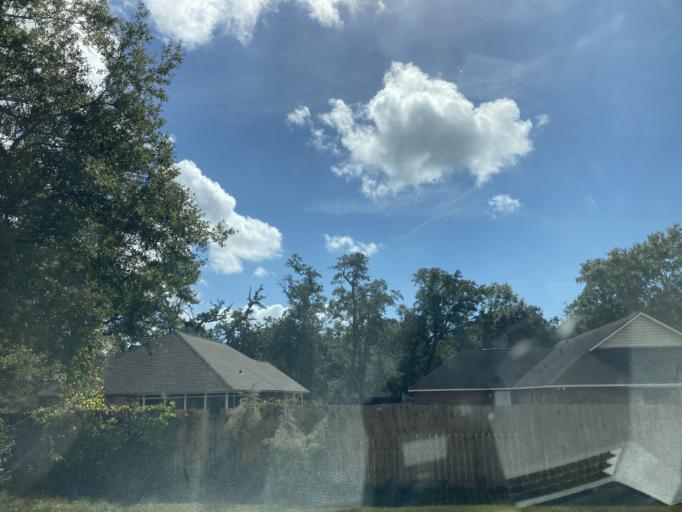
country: US
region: Mississippi
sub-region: Jackson County
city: Gulf Hills
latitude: 30.4511
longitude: -88.8314
